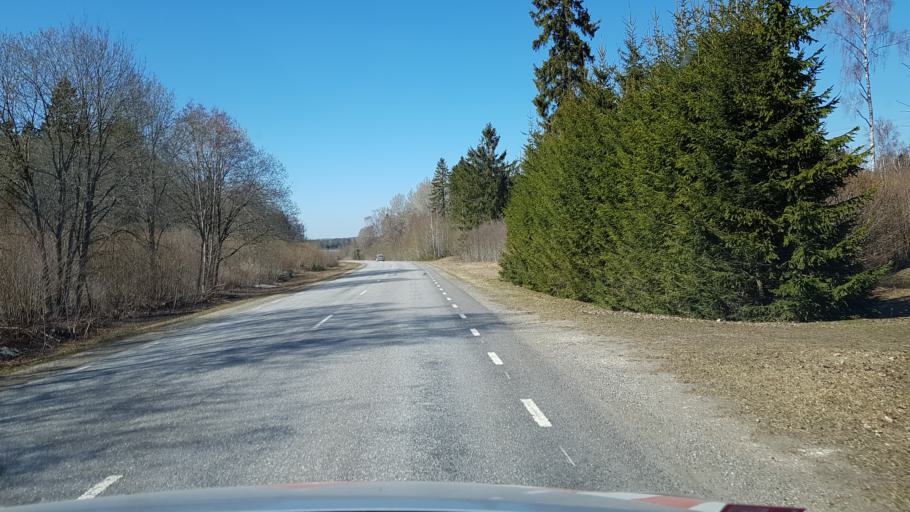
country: EE
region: Laeaene-Virumaa
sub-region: Vaeike-Maarja vald
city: Vaike-Maarja
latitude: 59.1527
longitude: 26.2196
